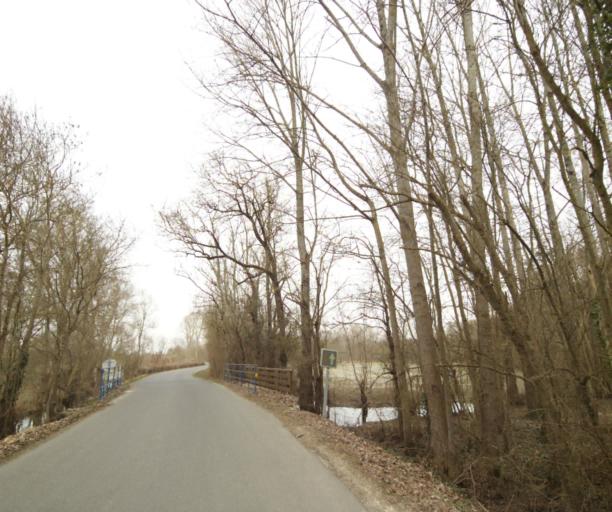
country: FR
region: Poitou-Charentes
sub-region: Departement des Deux-Sevres
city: Bessines
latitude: 46.3041
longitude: -0.5168
